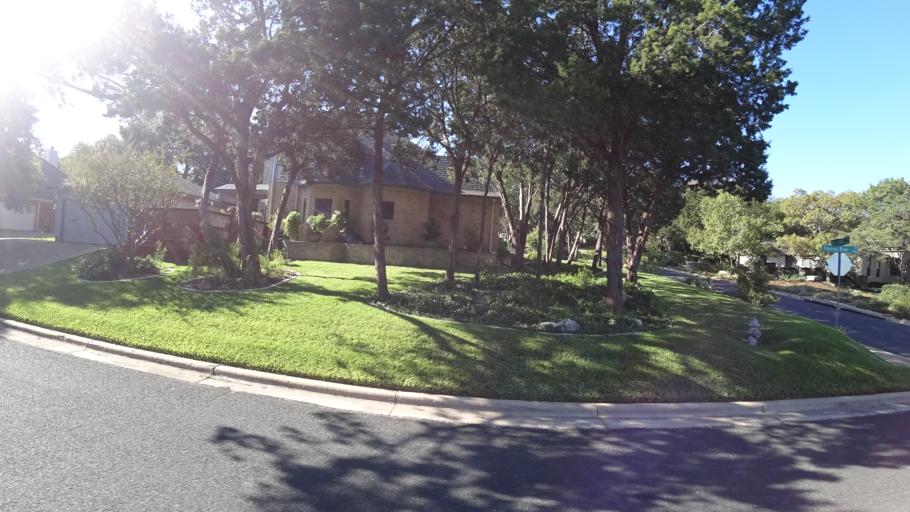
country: US
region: Texas
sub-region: Williamson County
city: Jollyville
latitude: 30.4112
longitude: -97.7600
